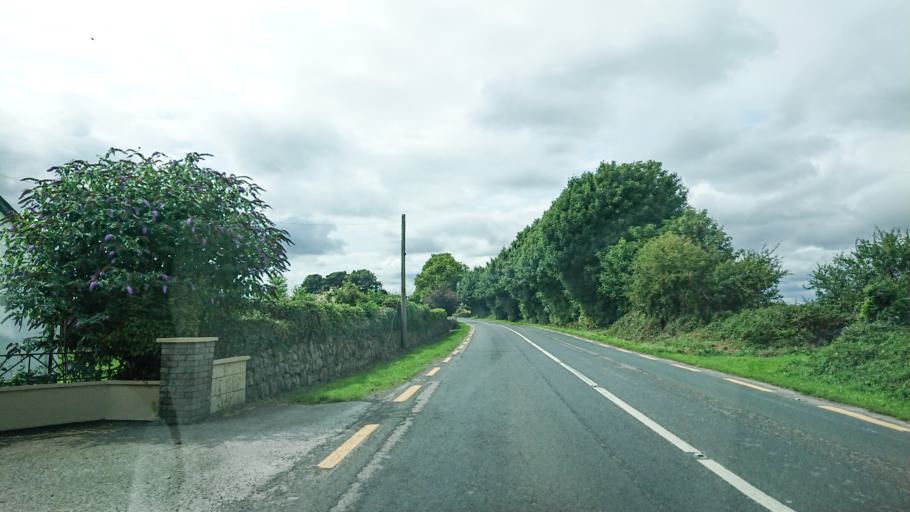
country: IE
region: Munster
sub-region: Waterford
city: Dungarvan
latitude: 52.1224
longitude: -7.7448
